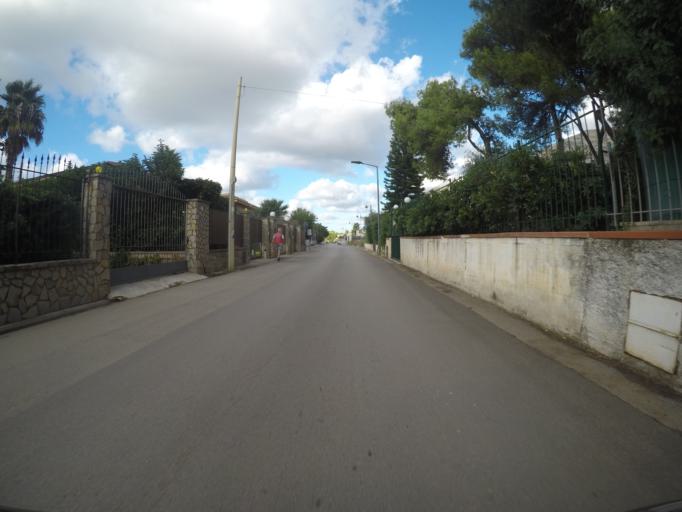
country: IT
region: Sicily
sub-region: Palermo
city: Isola delle Femmine
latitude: 38.1853
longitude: 13.2414
